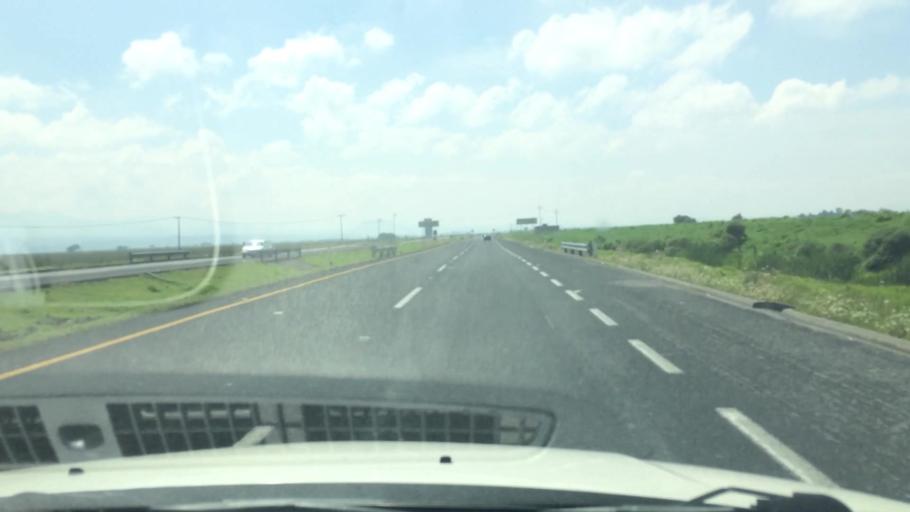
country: MX
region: Mexico
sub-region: Toluca
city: La Constitucion Toltepec
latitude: 19.3567
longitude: -99.5349
